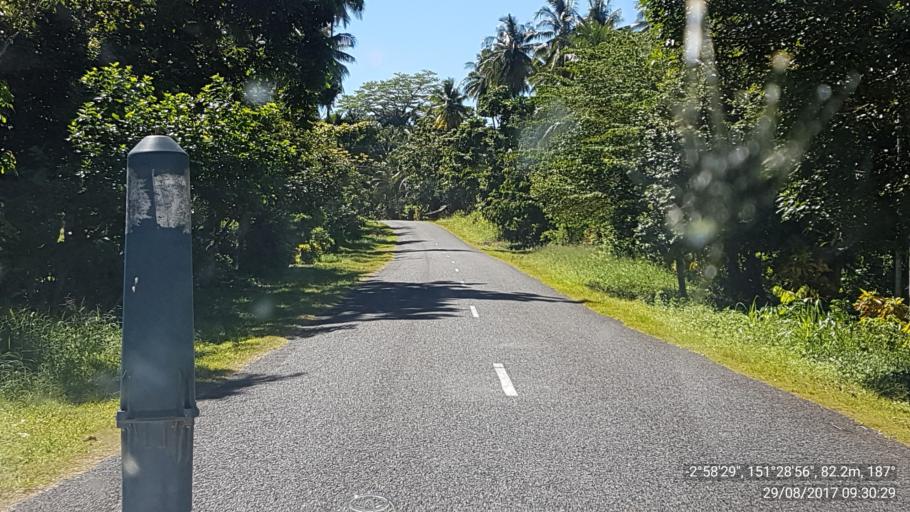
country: PG
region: New Ireland
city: Kavieng
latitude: -2.9747
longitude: 151.4825
